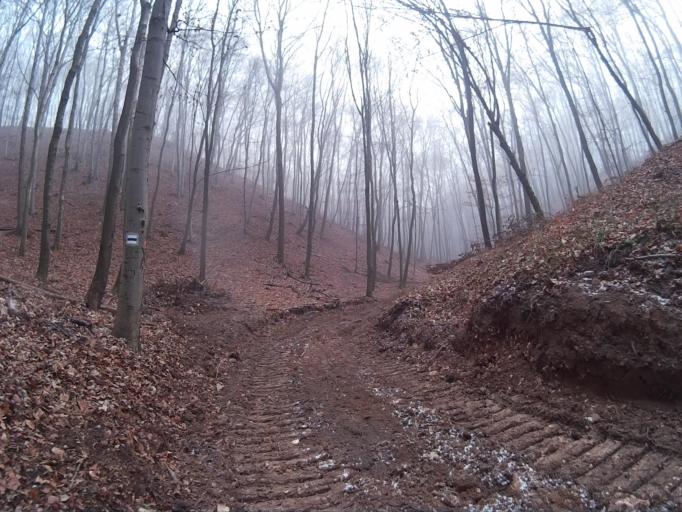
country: HU
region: Komarom-Esztergom
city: Oroszlany
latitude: 47.4553
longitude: 18.3952
